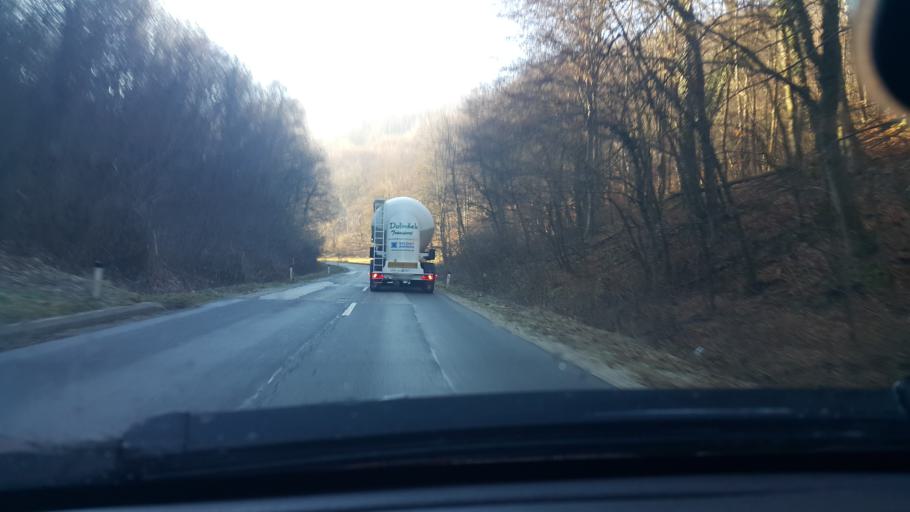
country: SI
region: Bistrica ob Sotli
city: Bistrica ob Sotli
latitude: 46.0401
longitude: 15.6873
